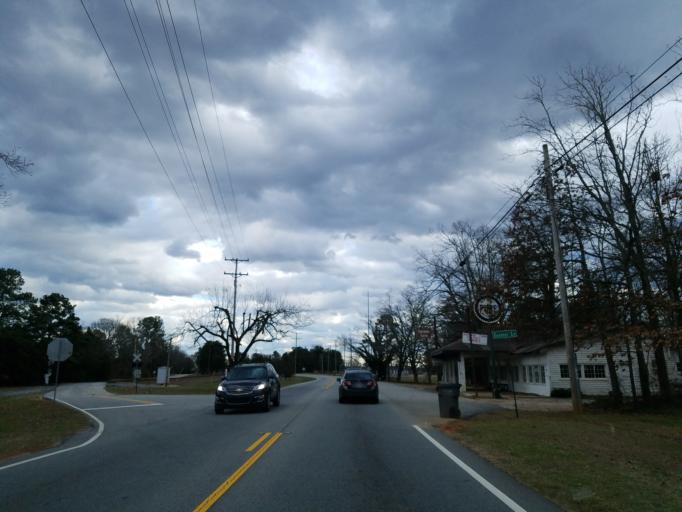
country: US
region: Georgia
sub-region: Henry County
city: Locust Grove
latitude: 33.3637
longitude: -84.1216
